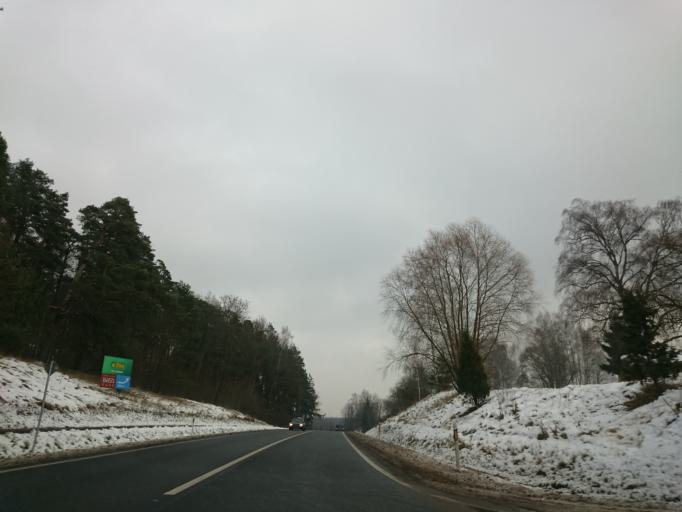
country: LV
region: Pargaujas
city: Stalbe
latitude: 57.3614
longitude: 24.9728
